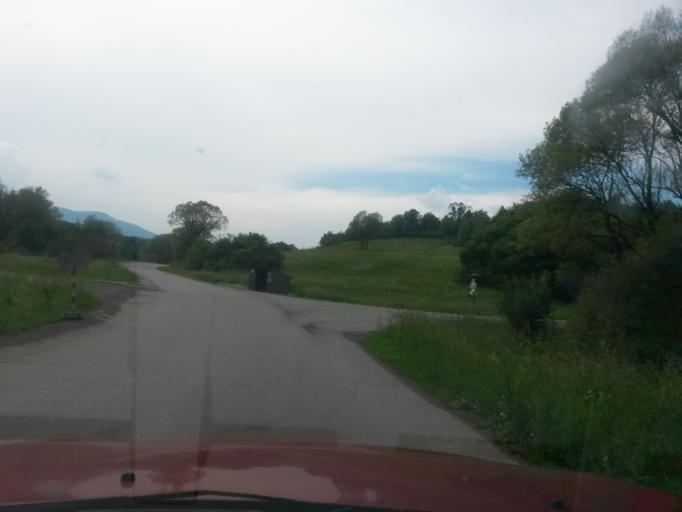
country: UA
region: Zakarpattia
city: Velykyi Bereznyi
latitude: 48.9290
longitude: 22.3617
